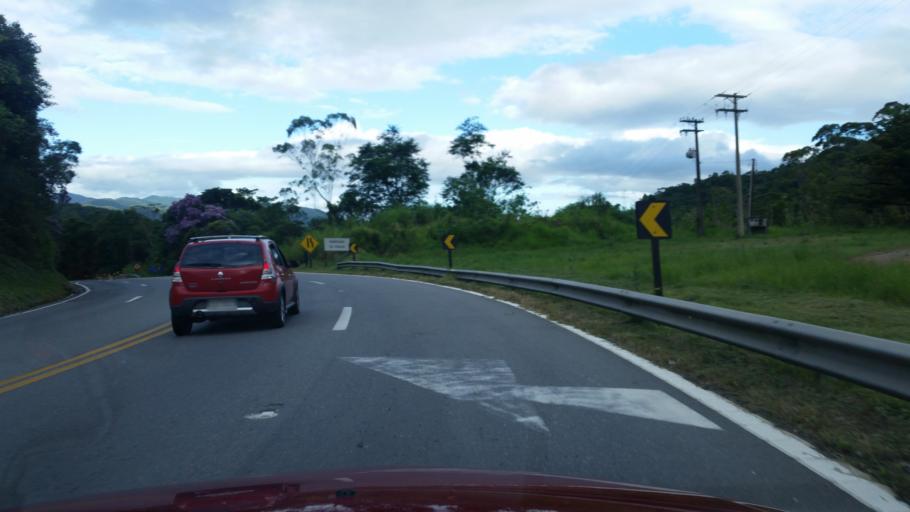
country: BR
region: Sao Paulo
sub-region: Miracatu
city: Miracatu
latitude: -24.2695
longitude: -47.2857
